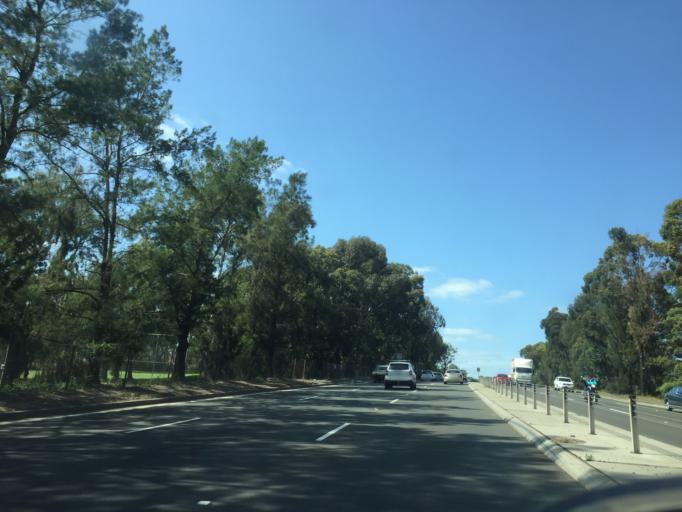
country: AU
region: New South Wales
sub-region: Strathfield
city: Homebush
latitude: -33.8732
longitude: 151.0664
